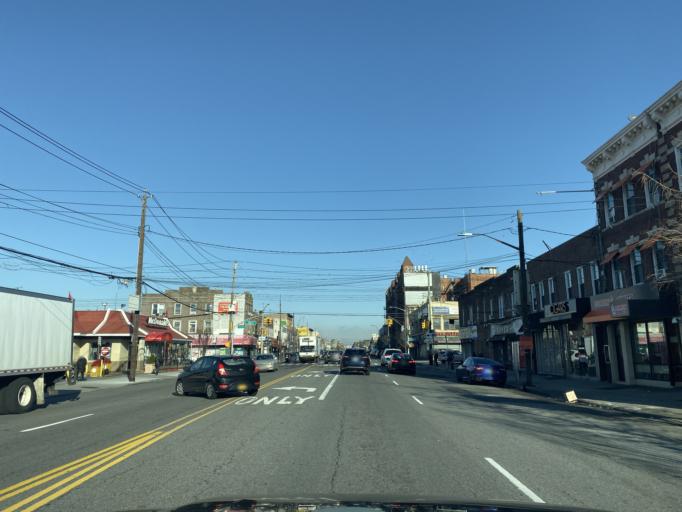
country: US
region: New York
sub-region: Kings County
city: Bensonhurst
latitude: 40.5977
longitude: -73.9611
